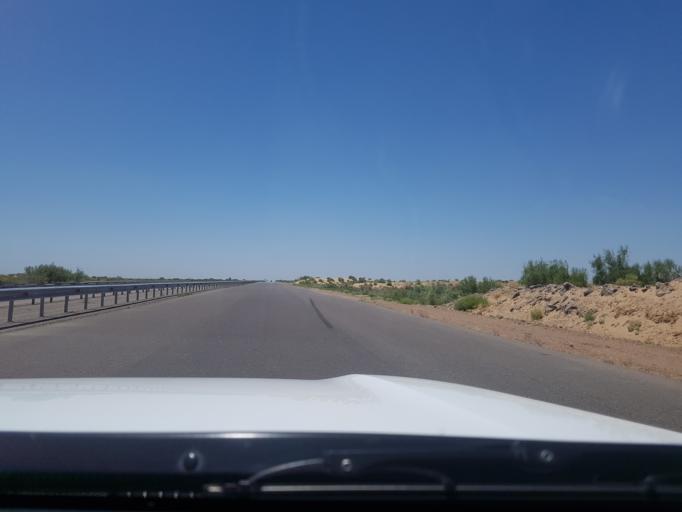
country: TM
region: Mary
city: Mary
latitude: 37.2910
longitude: 61.3417
